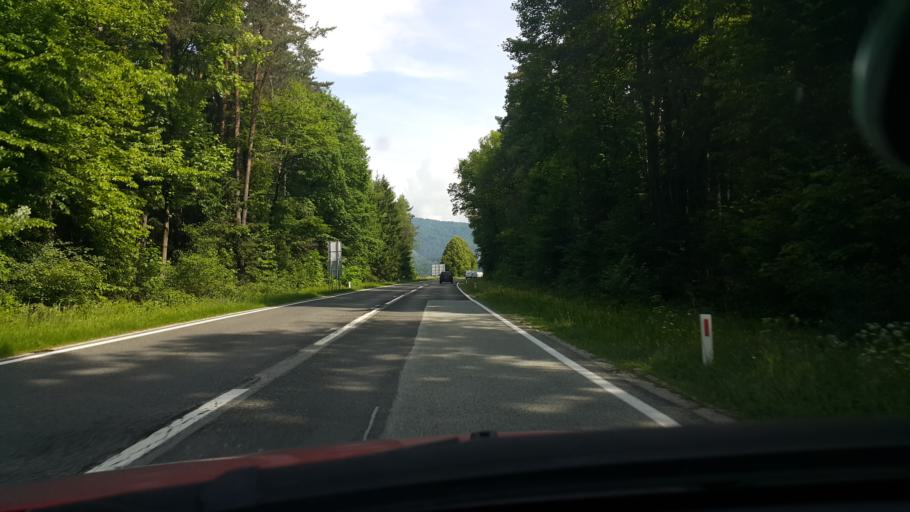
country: SI
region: Trzic
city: Bistrica pri Trzicu
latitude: 46.3203
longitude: 14.2784
